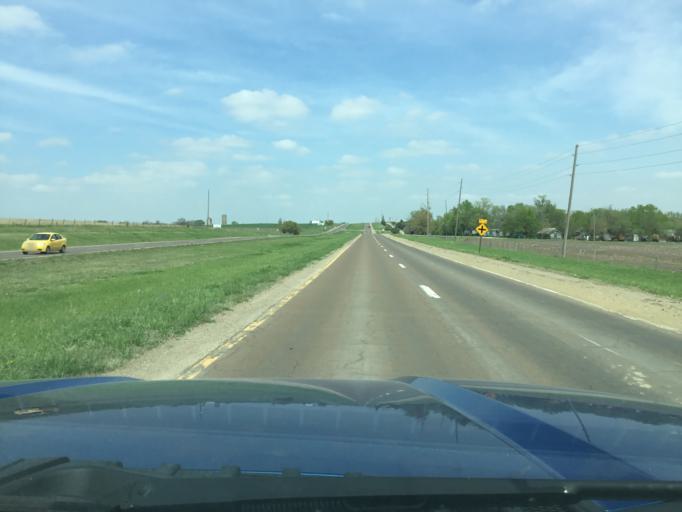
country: US
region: Kansas
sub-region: Osage County
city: Carbondale
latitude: 38.9113
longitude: -95.6874
